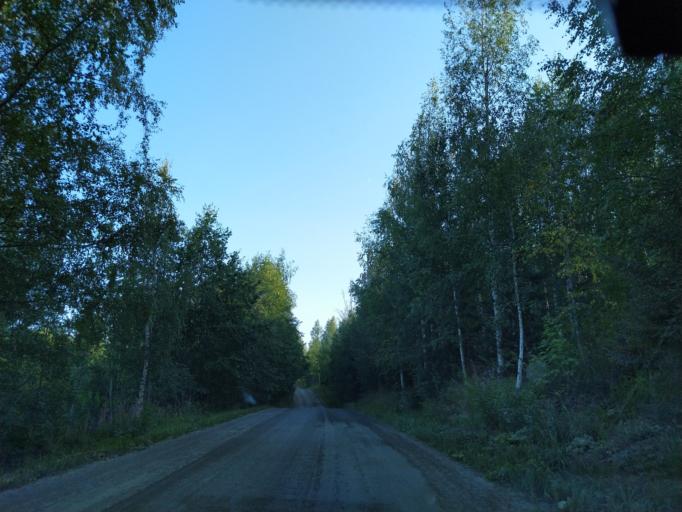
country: FI
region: Central Finland
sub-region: Jaemsae
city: Kuhmoinen
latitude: 61.6323
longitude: 25.0924
